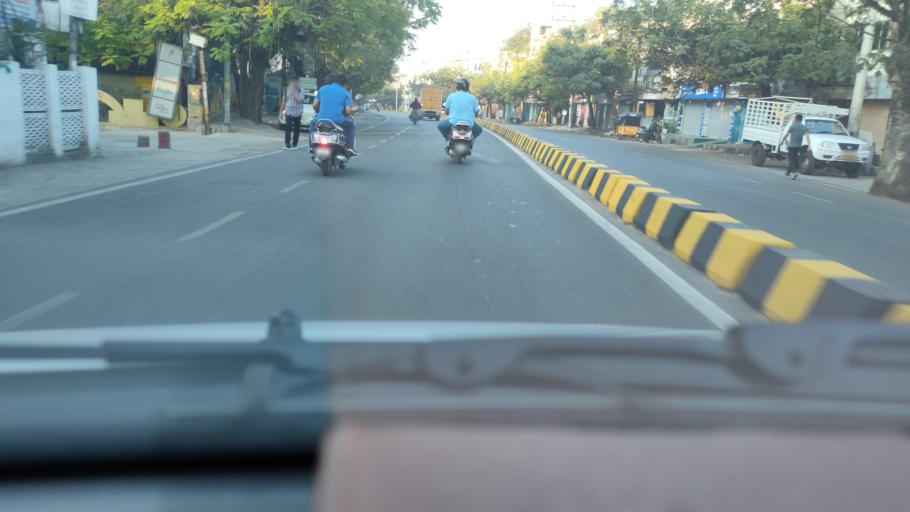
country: IN
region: Telangana
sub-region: Rangareddi
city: Gaddi Annaram
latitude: 17.4048
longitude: 78.5122
